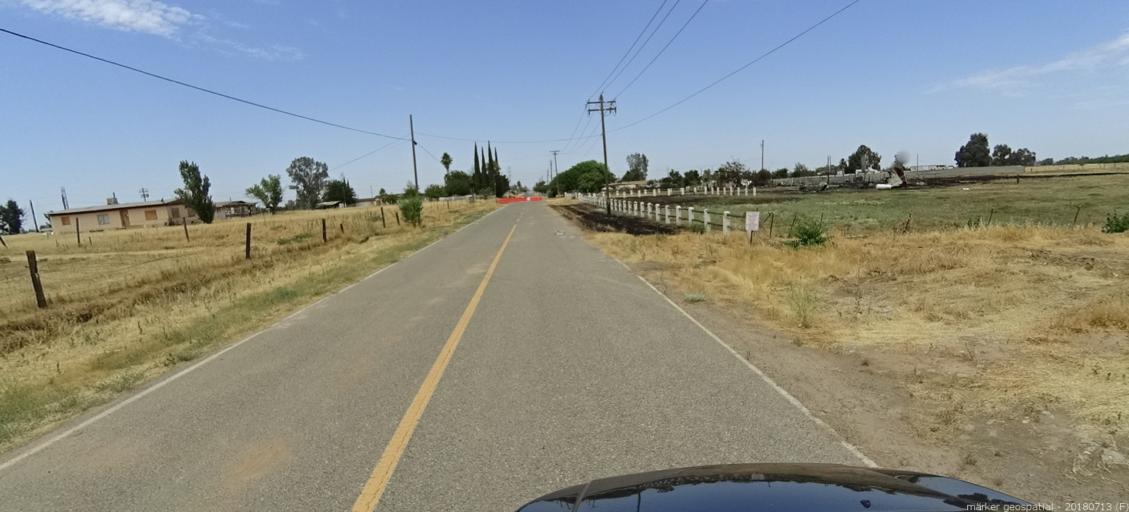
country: US
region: California
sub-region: Madera County
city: Madera Acres
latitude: 36.9962
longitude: -120.0442
